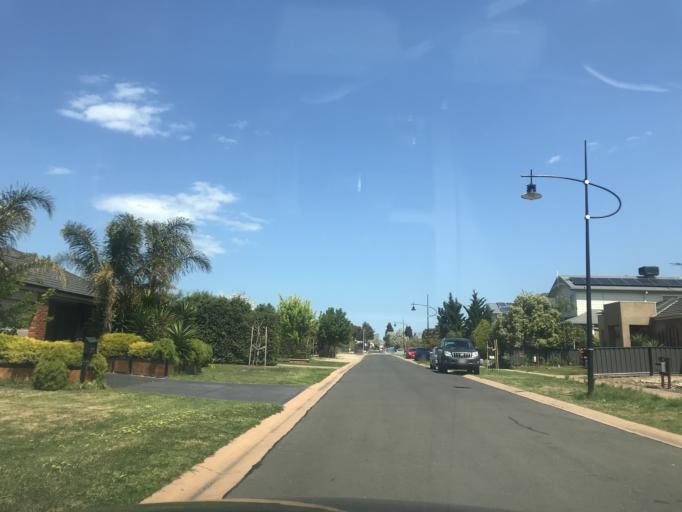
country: AU
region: Victoria
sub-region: Wyndham
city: Williams Landing
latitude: -37.8889
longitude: 144.7303
